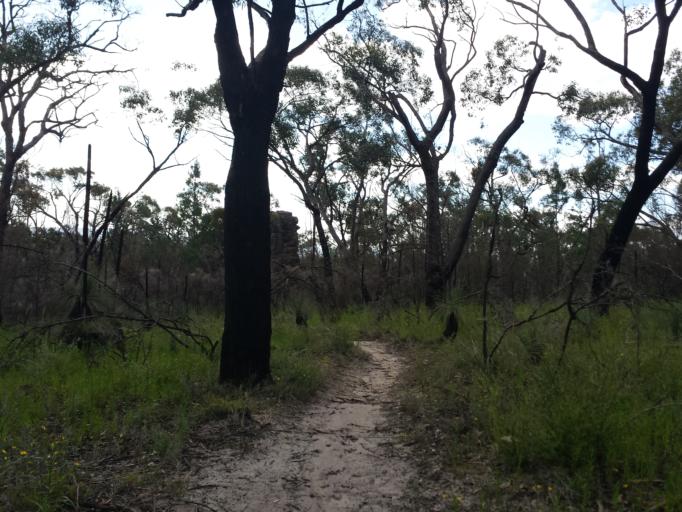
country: AU
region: Victoria
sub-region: Southern Grampians
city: Hamilton
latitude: -37.2719
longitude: 142.2738
